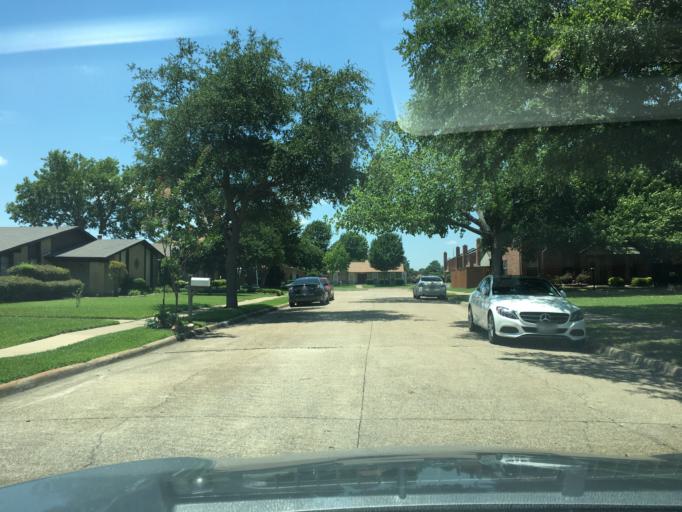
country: US
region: Texas
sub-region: Dallas County
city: Garland
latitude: 32.9500
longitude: -96.6765
